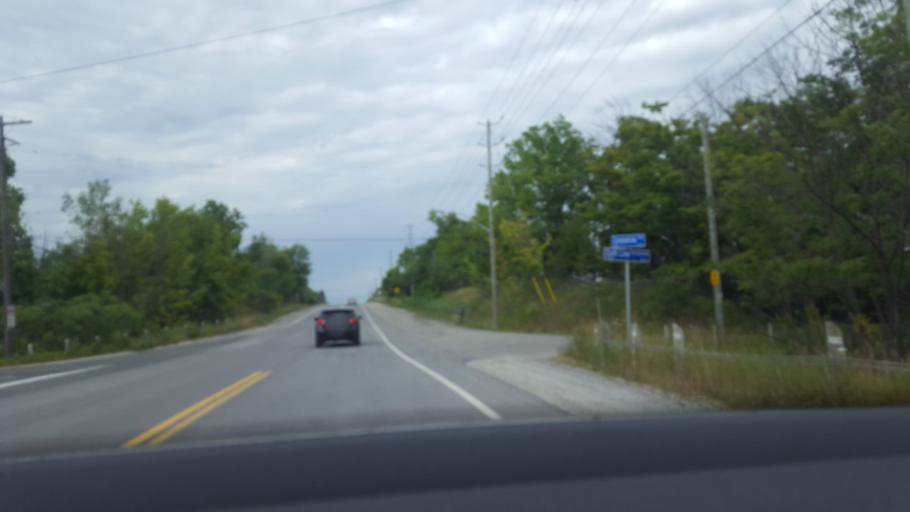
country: CA
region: Ontario
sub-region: Halton
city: Milton
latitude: 43.5156
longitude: -79.9495
